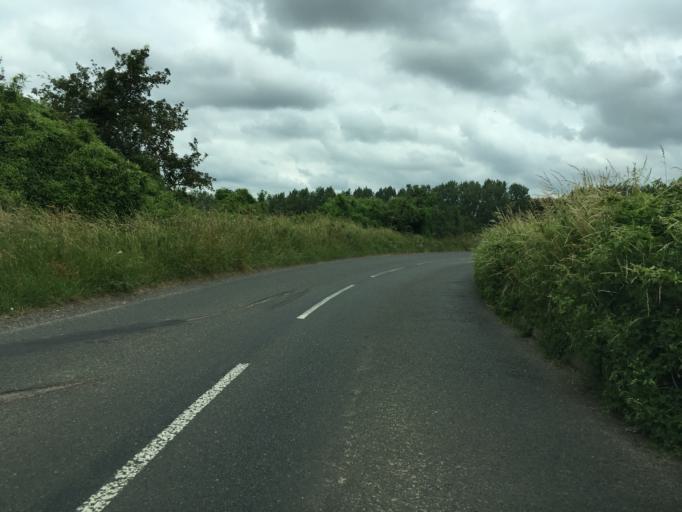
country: GB
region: England
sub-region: Oxfordshire
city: Charlbury
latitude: 51.9008
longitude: -1.4915
